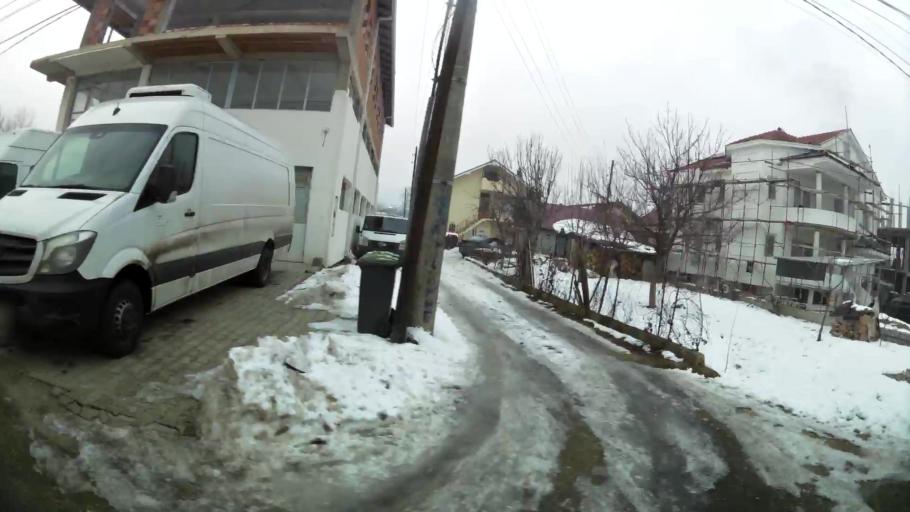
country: MK
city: Kondovo
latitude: 42.0458
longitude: 21.3507
